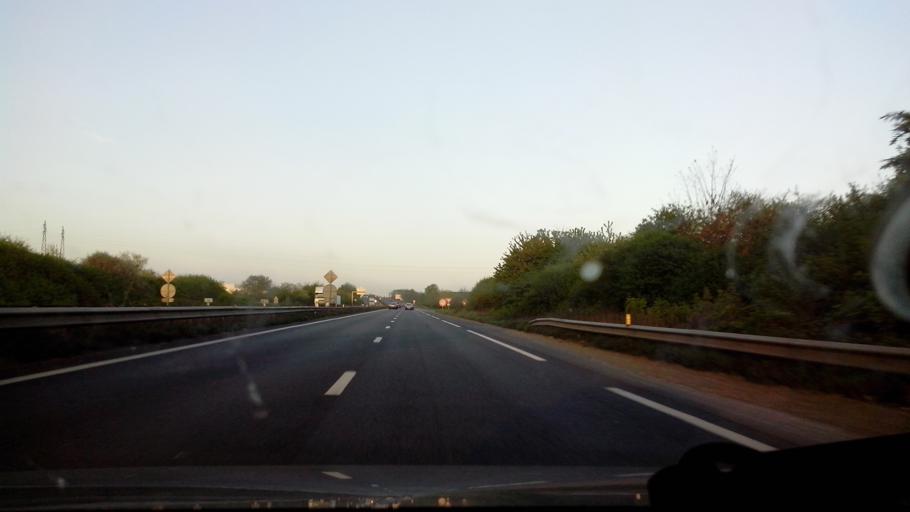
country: FR
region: Ile-de-France
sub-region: Departement de Seine-et-Marne
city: Lieusaint
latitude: 48.6453
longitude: 2.5496
